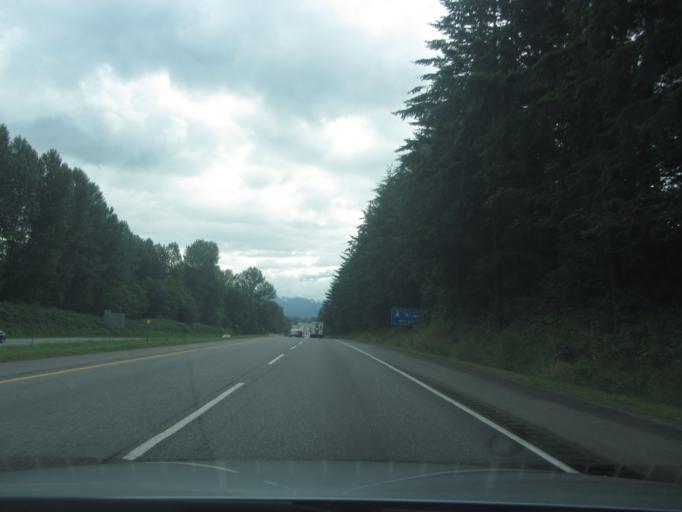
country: US
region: Washington
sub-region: Whatcom County
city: Sumas
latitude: 49.0334
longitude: -122.2807
